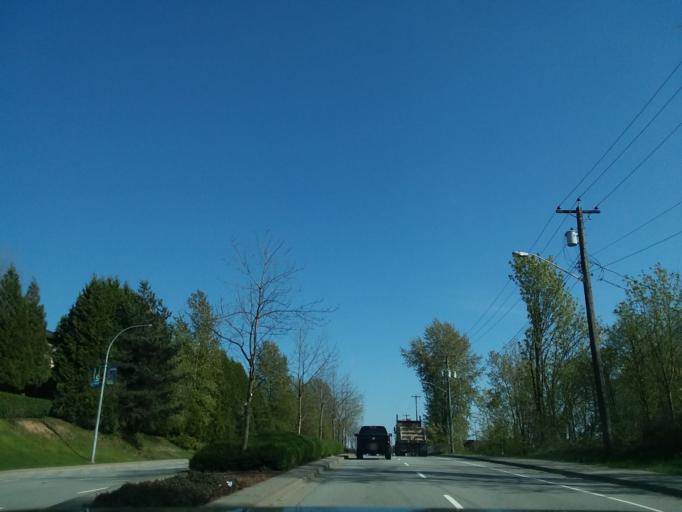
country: CA
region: British Columbia
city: New Westminster
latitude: 49.2446
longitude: -122.8905
